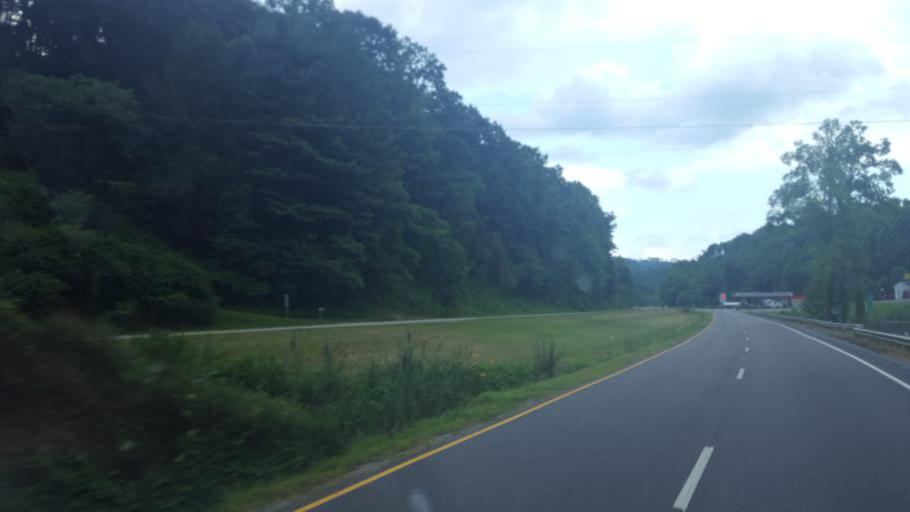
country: US
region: Virginia
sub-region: Wise County
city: Pound
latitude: 37.0920
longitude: -82.6002
